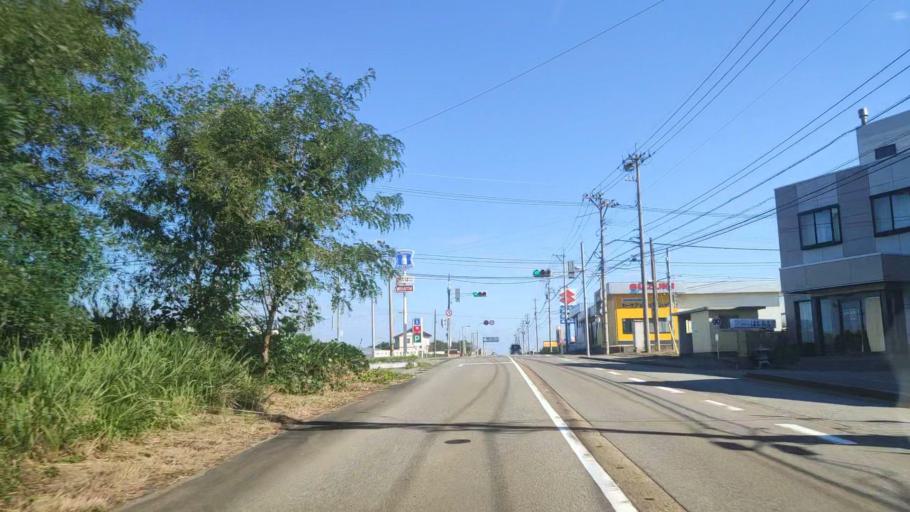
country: JP
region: Ishikawa
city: Hakui
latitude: 36.9875
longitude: 136.7759
